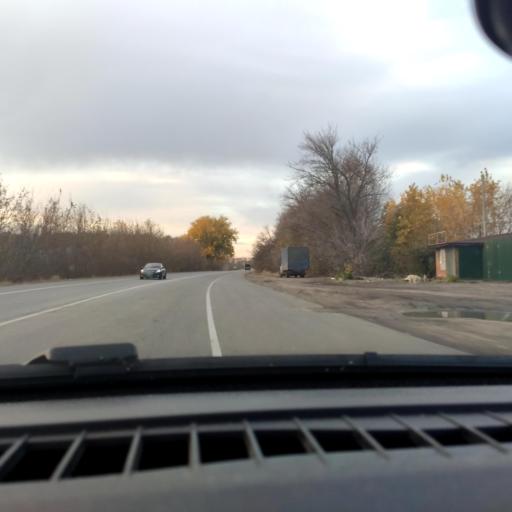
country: RU
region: Voronezj
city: Devitsa
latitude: 51.5983
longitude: 38.9738
